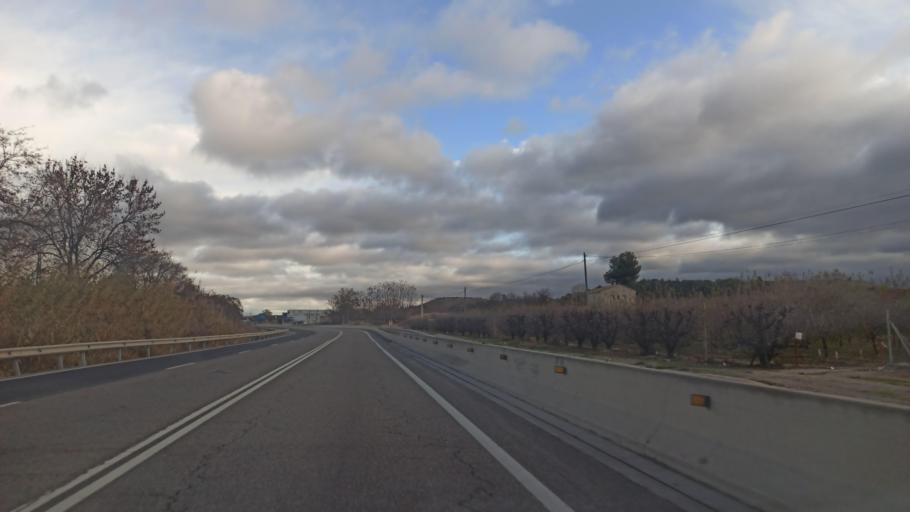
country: ES
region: Catalonia
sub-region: Provincia de Lleida
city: Alcoletge
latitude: 41.6350
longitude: 0.6698
